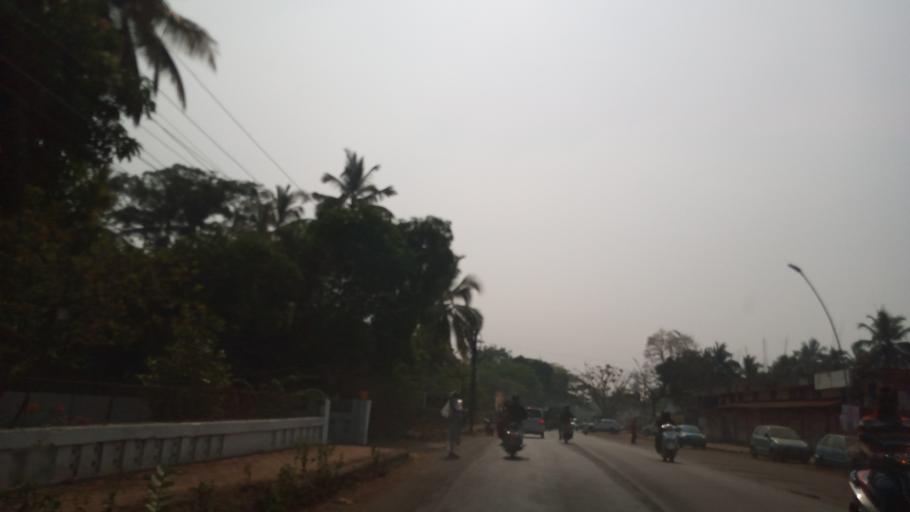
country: IN
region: Goa
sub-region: North Goa
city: Serula
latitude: 15.5331
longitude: 73.8229
